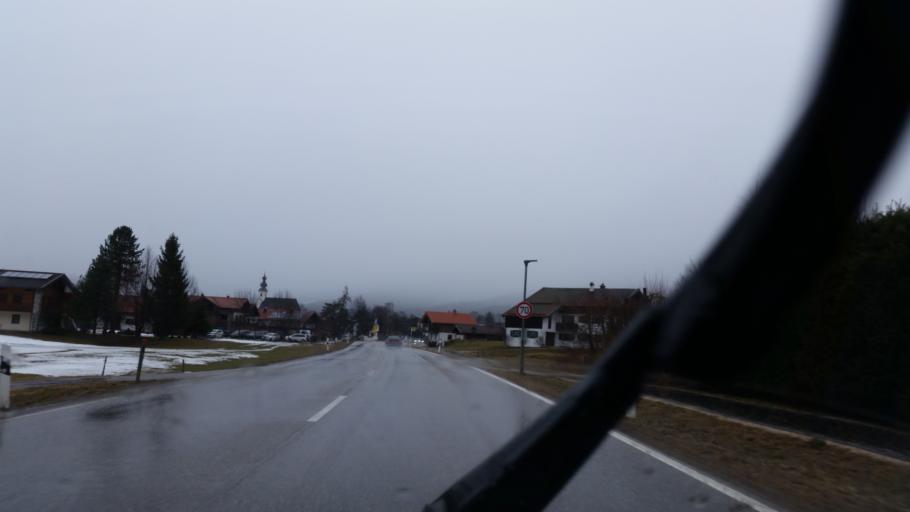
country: DE
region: Bavaria
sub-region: Upper Bavaria
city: Inzell
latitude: 47.7566
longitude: 12.7503
